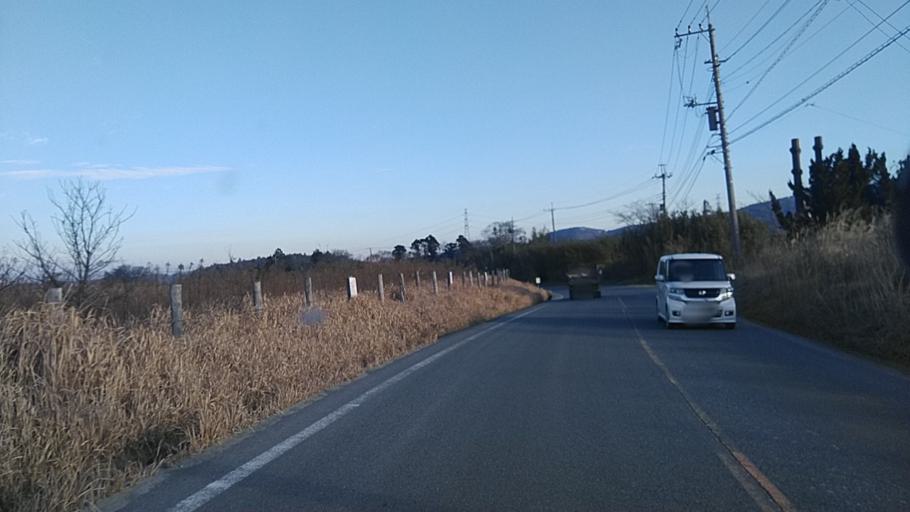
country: JP
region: Chiba
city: Kimitsu
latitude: 35.2719
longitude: 139.9893
